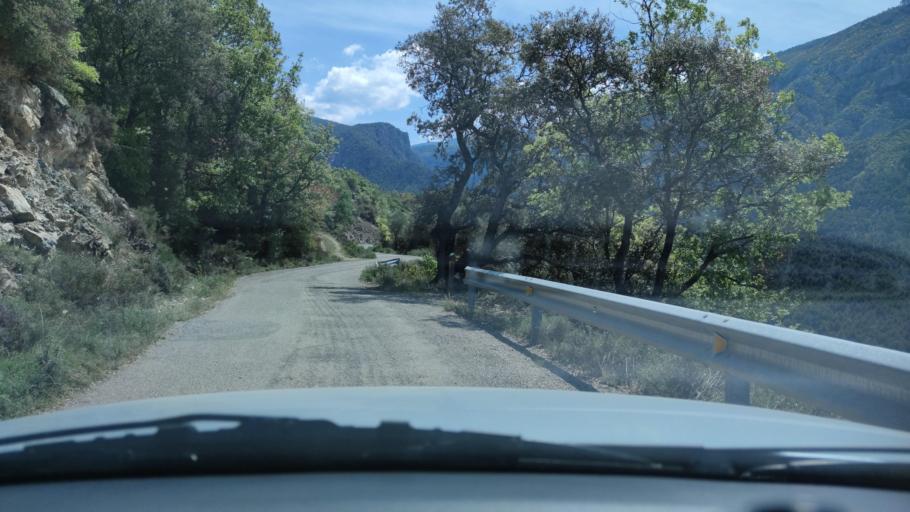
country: ES
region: Catalonia
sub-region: Provincia de Lleida
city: Sort
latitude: 42.3117
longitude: 1.0728
